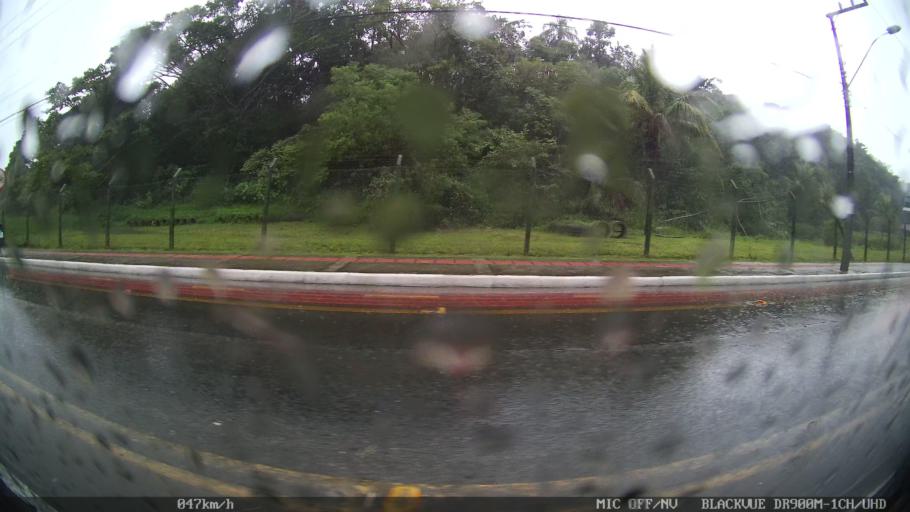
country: BR
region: Santa Catarina
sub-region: Balneario Camboriu
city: Balneario Camboriu
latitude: -26.9631
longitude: -48.6317
